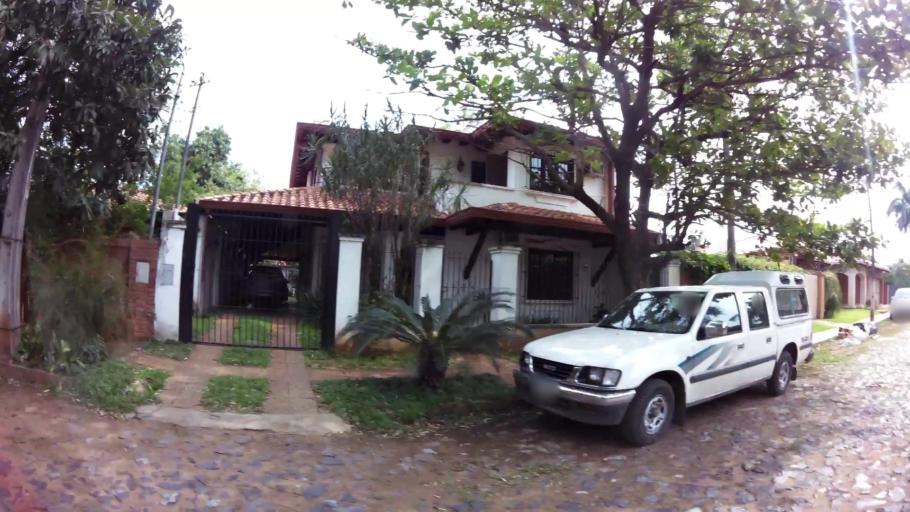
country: PY
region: Central
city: Fernando de la Mora
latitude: -25.2898
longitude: -57.5601
